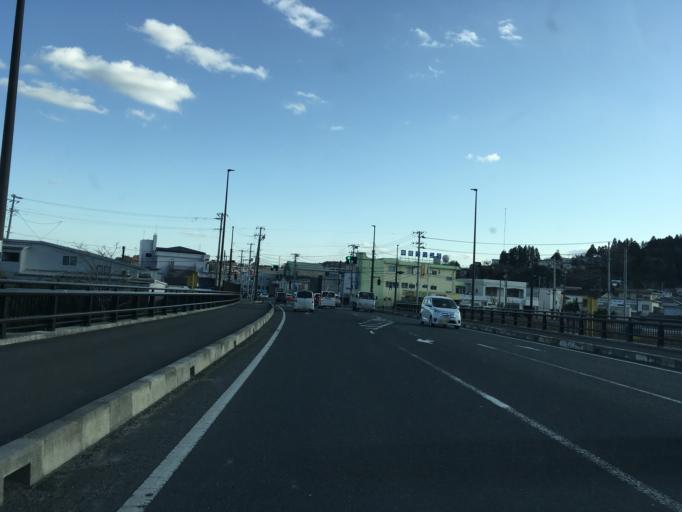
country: JP
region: Iwate
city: Ofunato
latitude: 38.9010
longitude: 141.5642
